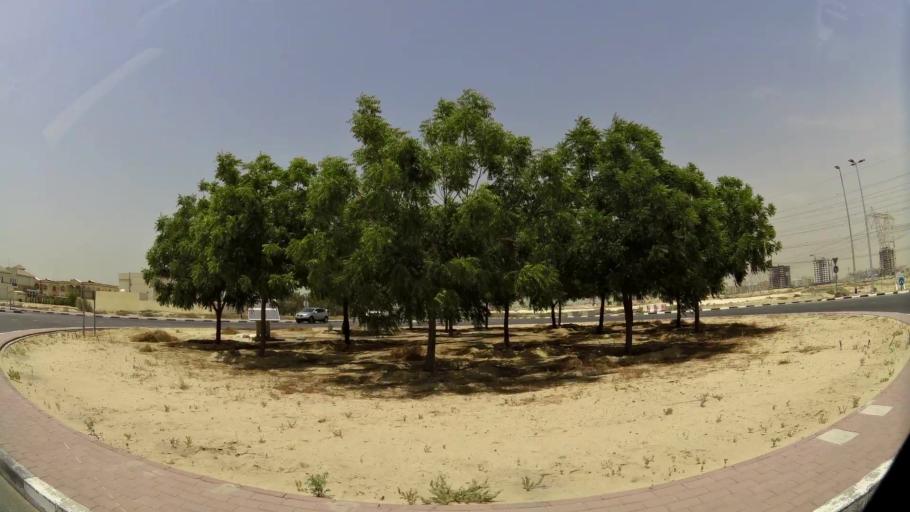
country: AE
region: Ash Shariqah
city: Sharjah
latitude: 25.1884
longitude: 55.3871
